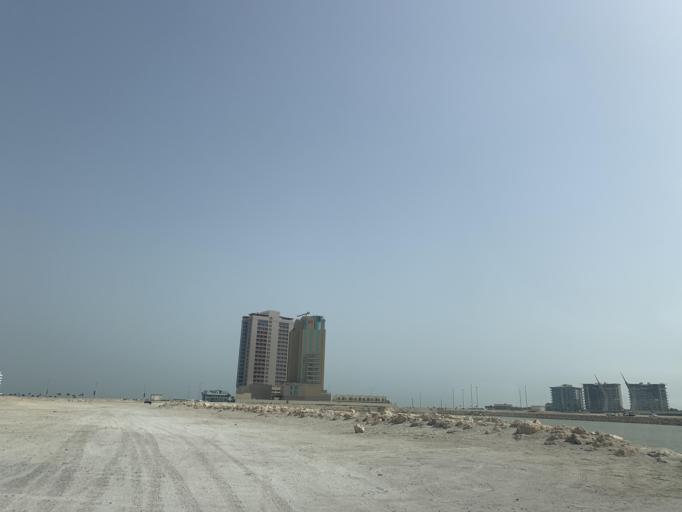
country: BH
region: Manama
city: Jidd Hafs
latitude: 26.2376
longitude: 50.5574
